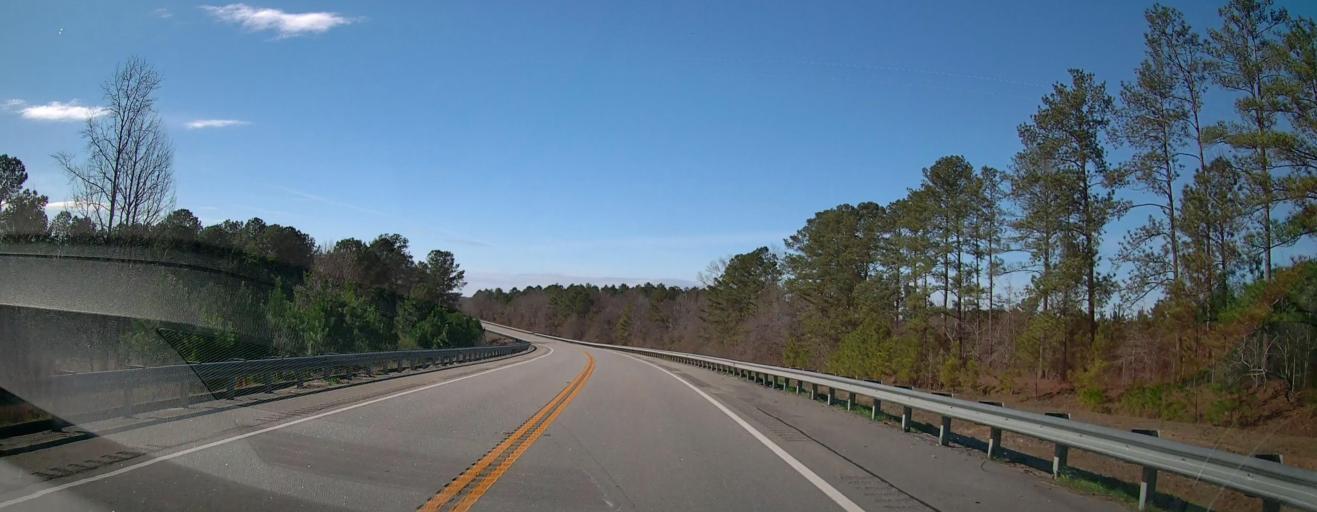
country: US
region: Georgia
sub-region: Macon County
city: Oglethorpe
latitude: 32.3440
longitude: -84.1353
